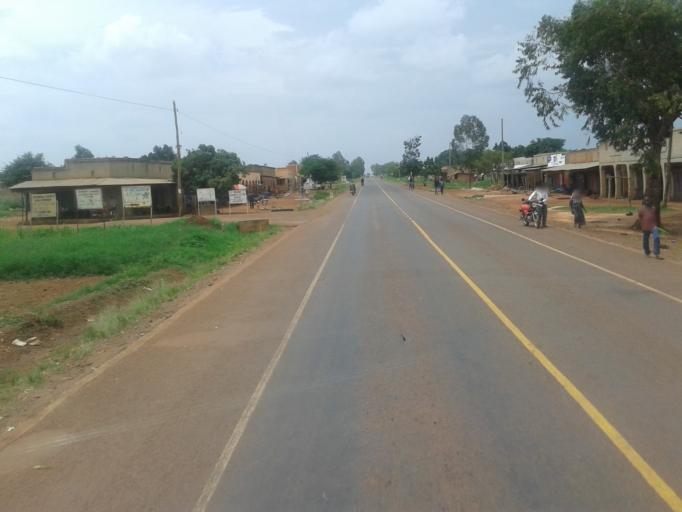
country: UG
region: Western Region
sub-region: Kiryandongo District
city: Kiryandongo
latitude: 1.9621
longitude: 32.1485
